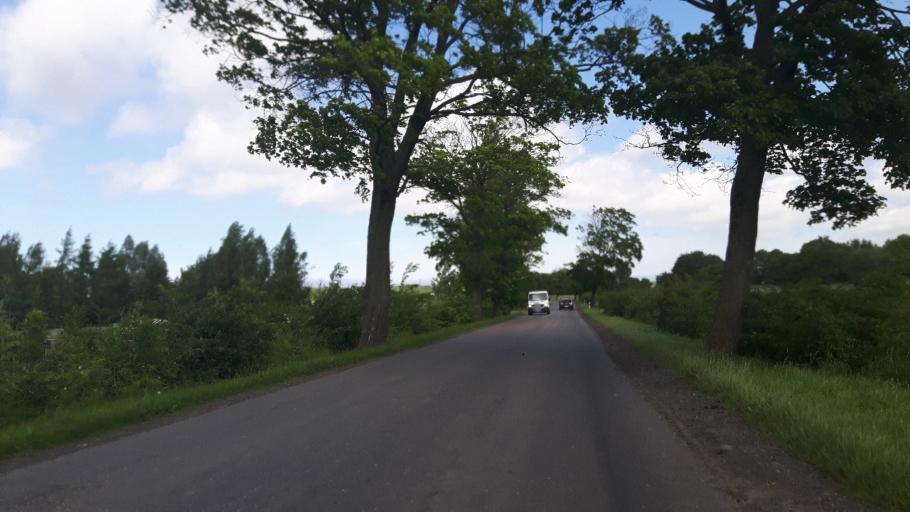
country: PL
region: Pomeranian Voivodeship
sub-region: Powiat slupski
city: Ustka
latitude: 54.5491
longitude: 16.8318
